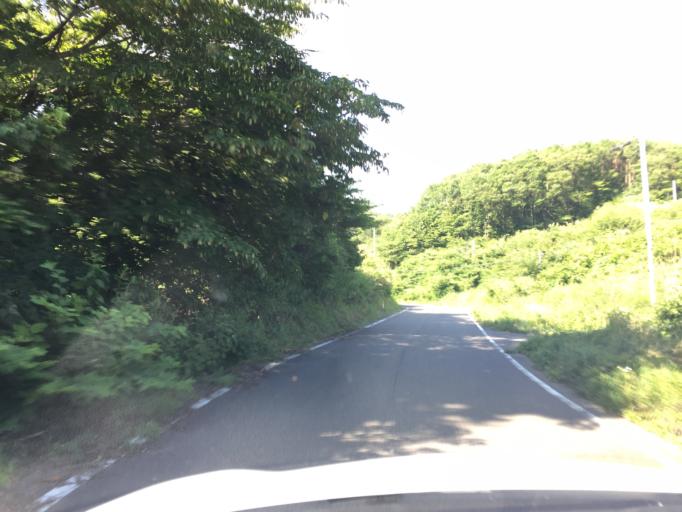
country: JP
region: Fukushima
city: Ishikawa
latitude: 37.2550
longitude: 140.4976
